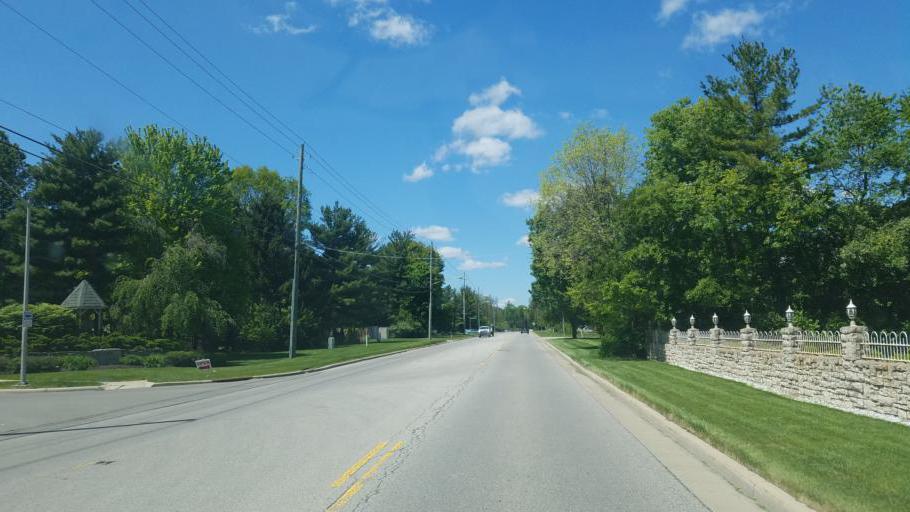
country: US
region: Ohio
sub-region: Franklin County
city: Dublin
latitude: 40.0570
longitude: -83.1083
